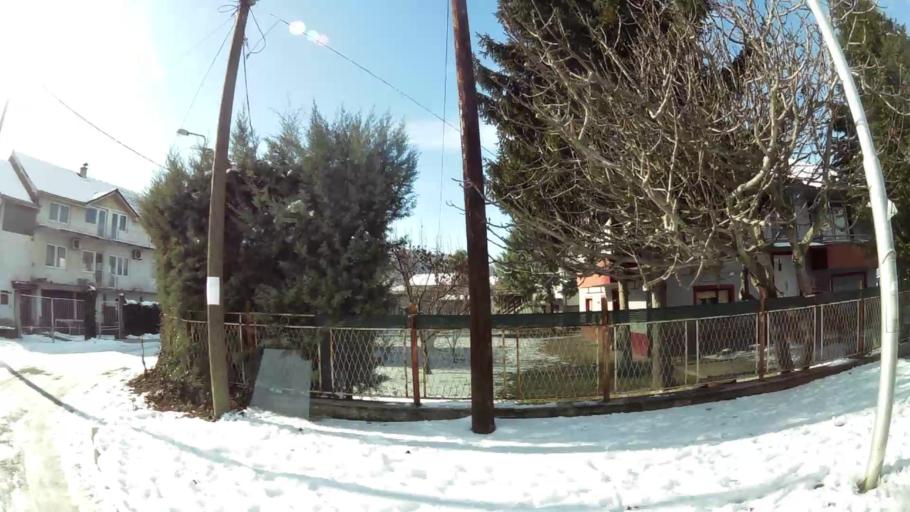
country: MK
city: Krushopek
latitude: 41.9989
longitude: 21.3707
